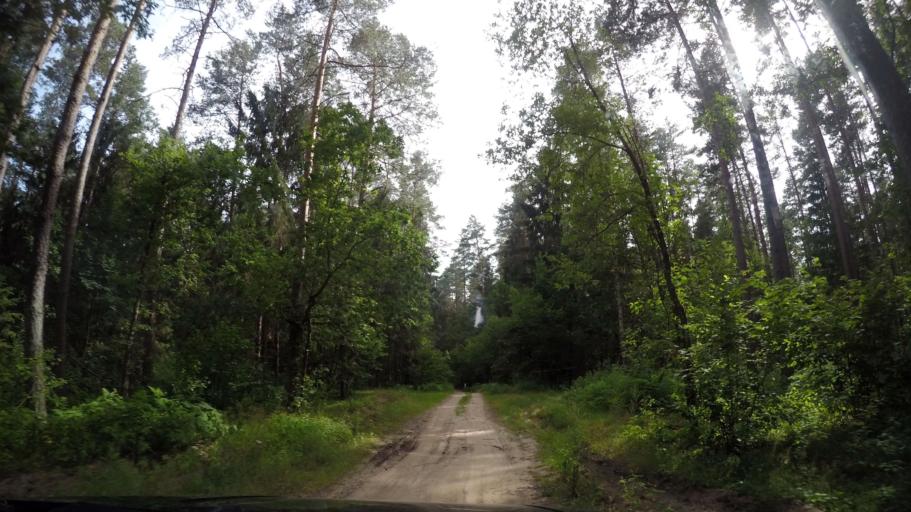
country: BY
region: Grodnenskaya
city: Skidal'
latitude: 53.8358
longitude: 24.1768
